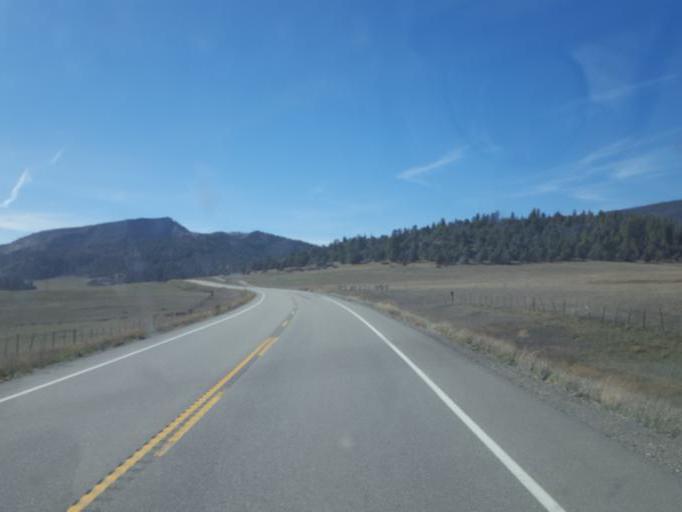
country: US
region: Colorado
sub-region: Archuleta County
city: Pagosa Springs
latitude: 37.2298
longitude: -107.1994
